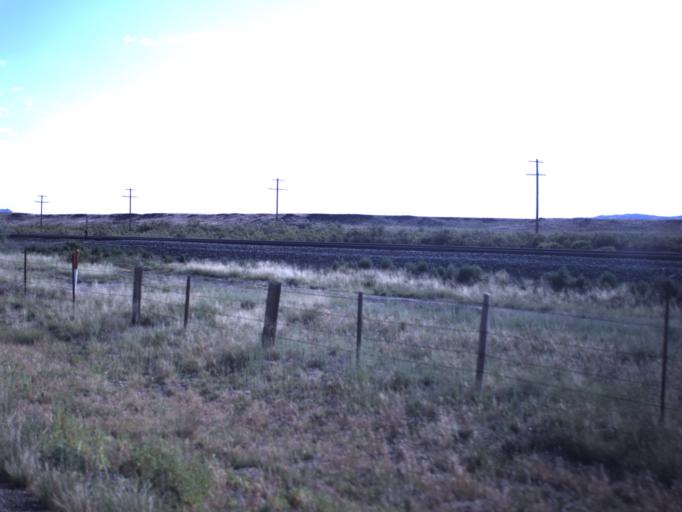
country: US
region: Utah
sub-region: Beaver County
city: Milford
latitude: 38.7110
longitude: -112.9697
